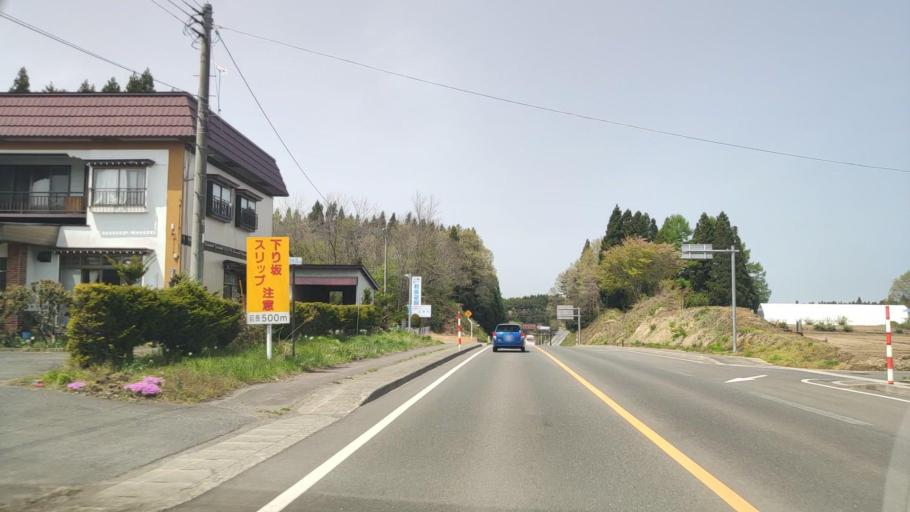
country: JP
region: Aomori
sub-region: Misawa Shi
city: Inuotose
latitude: 40.6602
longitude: 141.1906
